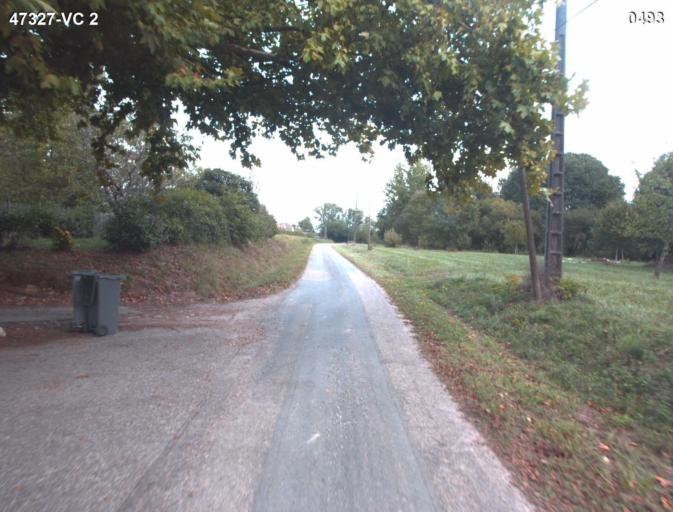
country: FR
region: Aquitaine
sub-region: Departement du Lot-et-Garonne
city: Barbaste
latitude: 44.1932
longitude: 0.2498
